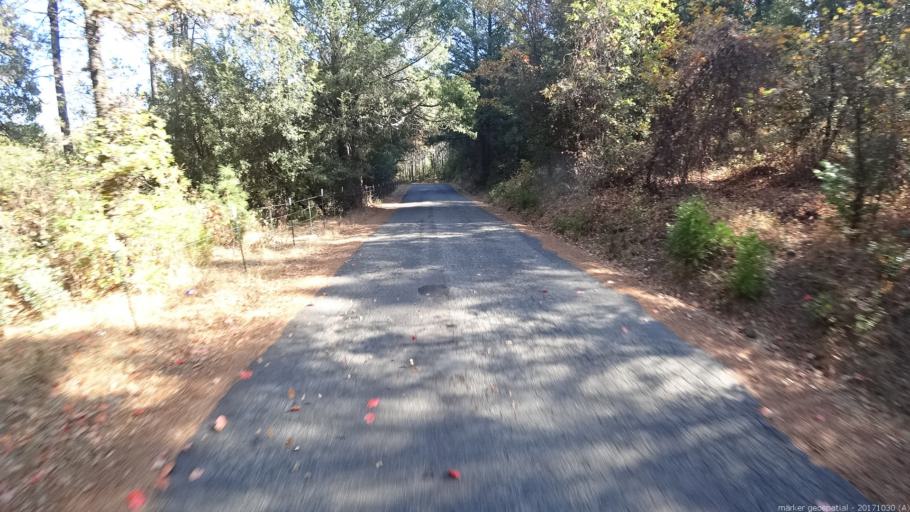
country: US
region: California
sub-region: Shasta County
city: Shingletown
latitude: 40.5672
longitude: -121.8851
